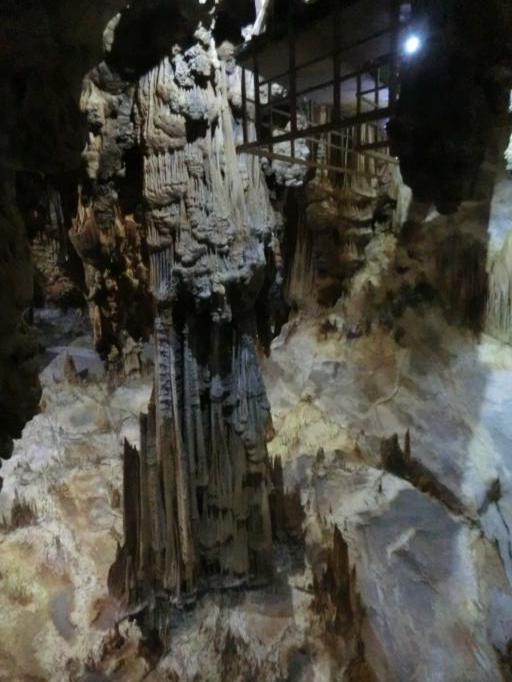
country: VN
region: Quang Binh
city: Ba Don
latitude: 17.5778
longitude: 106.2813
